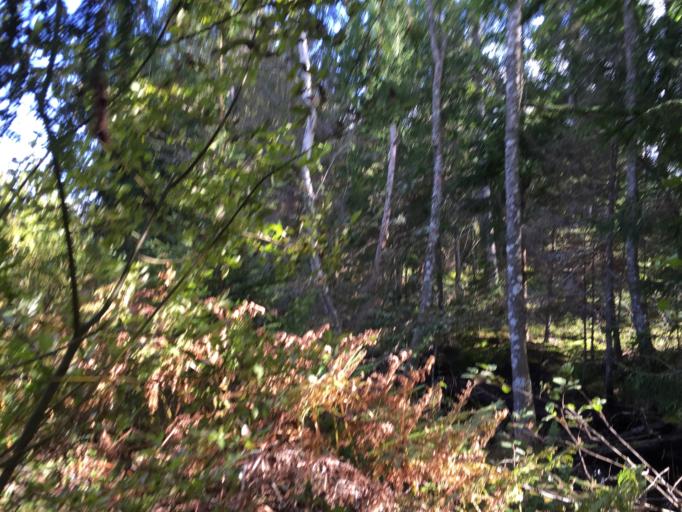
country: LV
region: Kuldigas Rajons
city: Kuldiga
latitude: 57.0020
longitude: 21.7973
